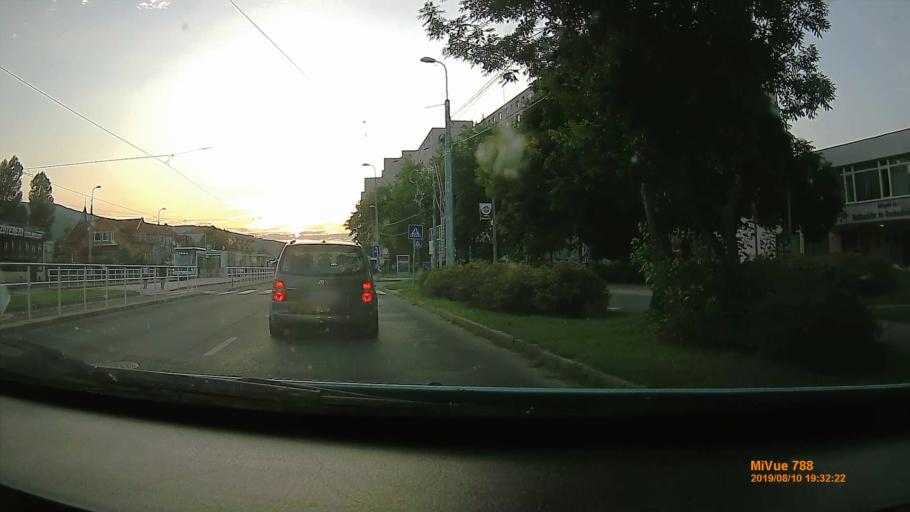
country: HU
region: Borsod-Abauj-Zemplen
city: Sajobabony
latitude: 48.1014
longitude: 20.6897
